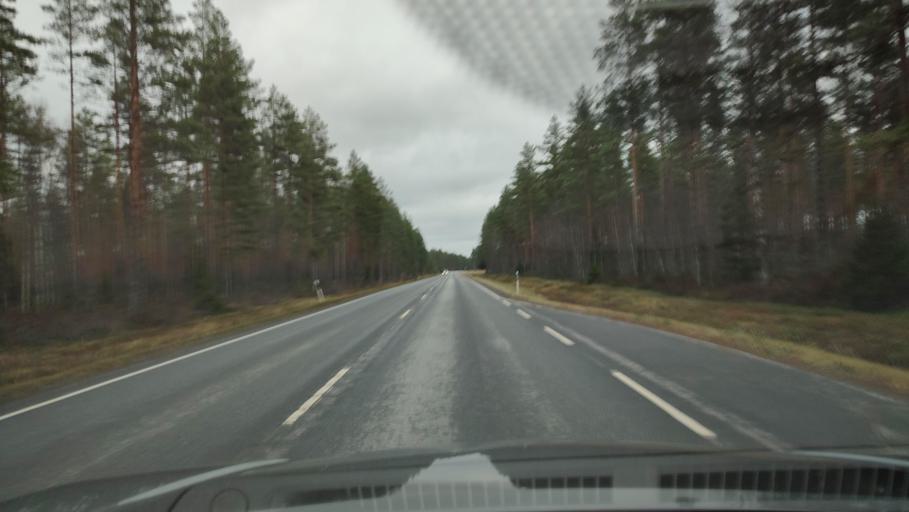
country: FI
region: Southern Ostrobothnia
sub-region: Suupohja
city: Kauhajoki
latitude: 62.5113
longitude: 22.3100
